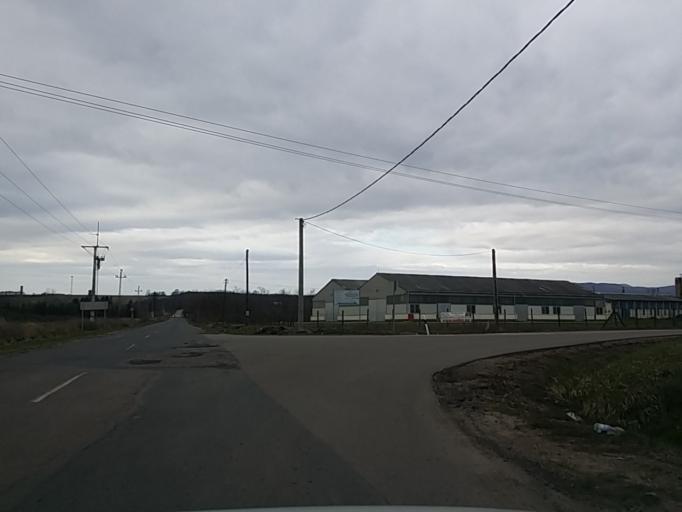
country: HU
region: Heves
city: Verpelet
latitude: 47.8527
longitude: 20.2122
